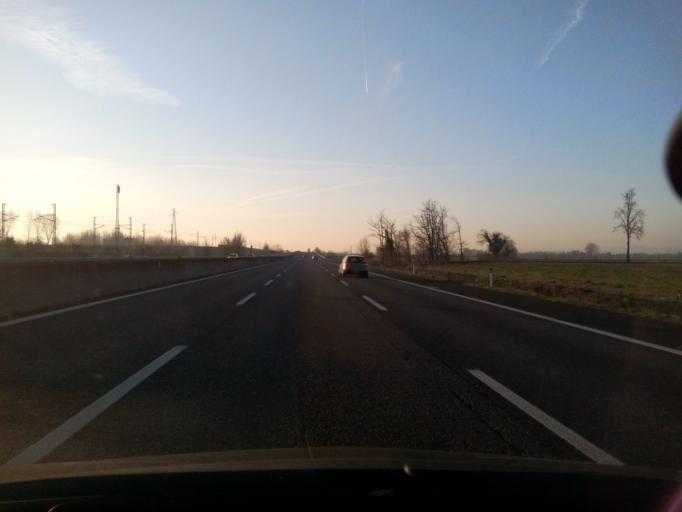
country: IT
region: Lombardy
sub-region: Provincia di Lodi
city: Villanova del Sillaro
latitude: 45.2425
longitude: 9.4942
